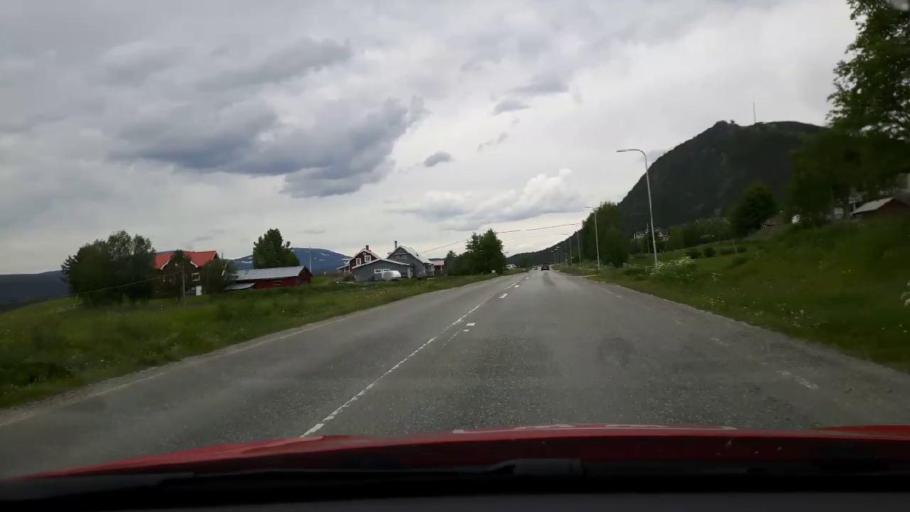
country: NO
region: Hedmark
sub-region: Engerdal
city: Engerdal
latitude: 62.5375
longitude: 12.5554
